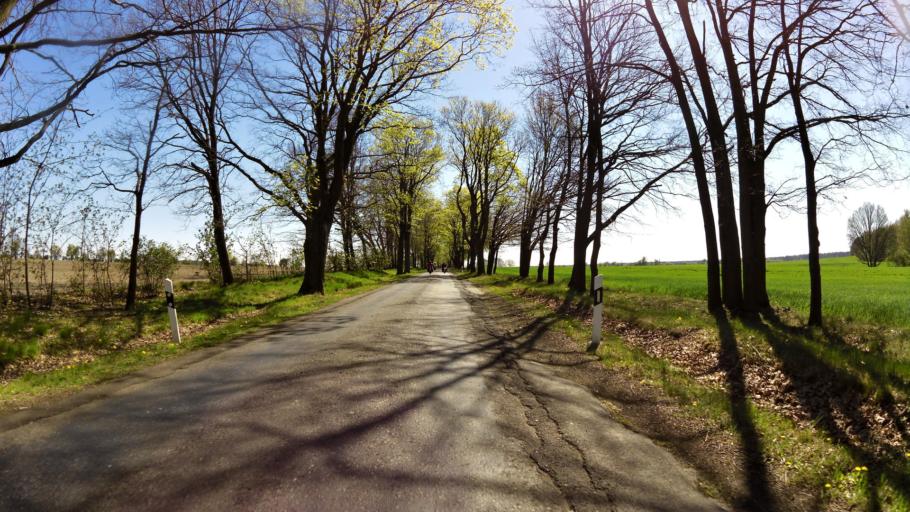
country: DE
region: Brandenburg
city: Strausberg
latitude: 52.6180
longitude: 13.8462
